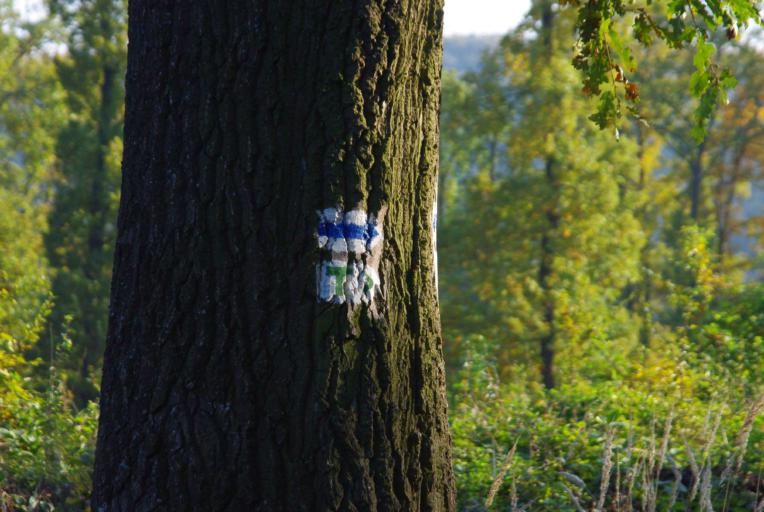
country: HU
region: Pest
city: Nagymaros
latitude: 47.8225
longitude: 18.9389
